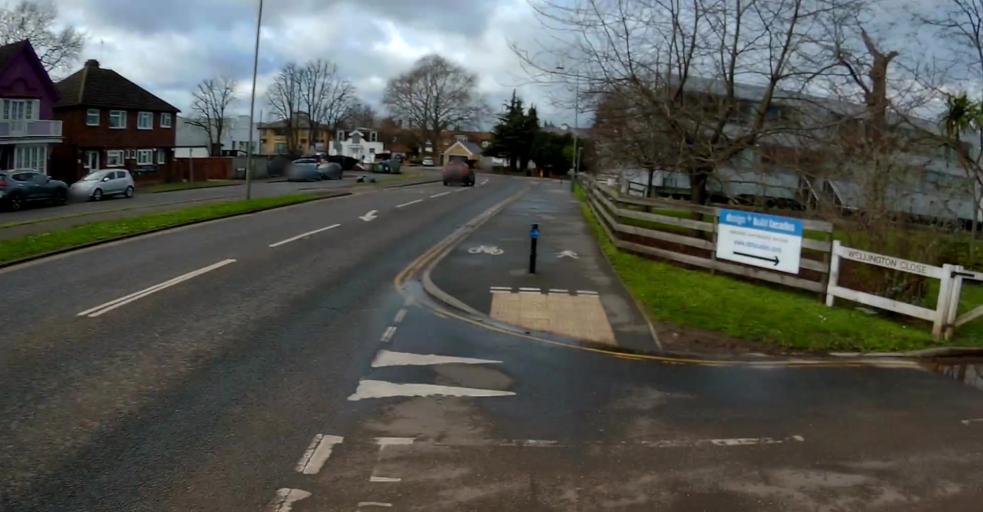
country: GB
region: England
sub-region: Surrey
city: Walton-on-Thames
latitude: 51.3859
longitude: -0.4234
